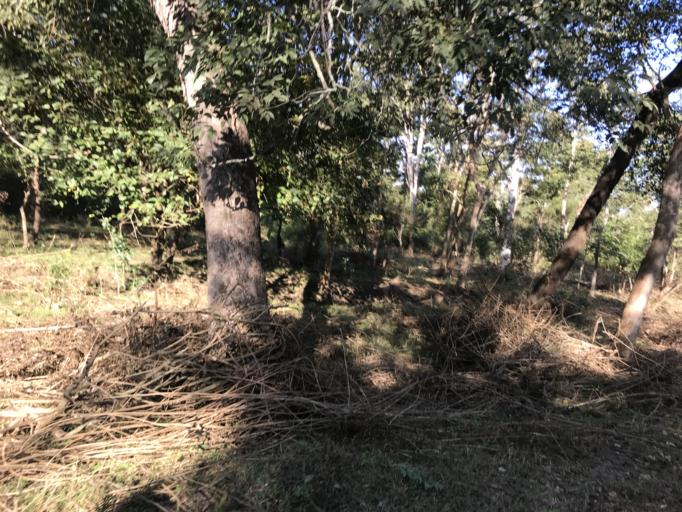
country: IN
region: Karnataka
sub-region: Mysore
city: Heggadadevankote
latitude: 11.9786
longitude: 76.2369
